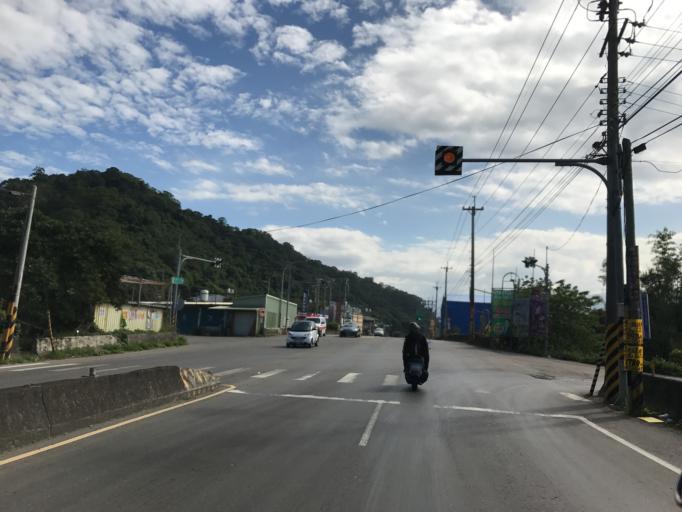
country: TW
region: Taiwan
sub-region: Hsinchu
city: Zhubei
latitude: 24.7442
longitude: 121.1044
